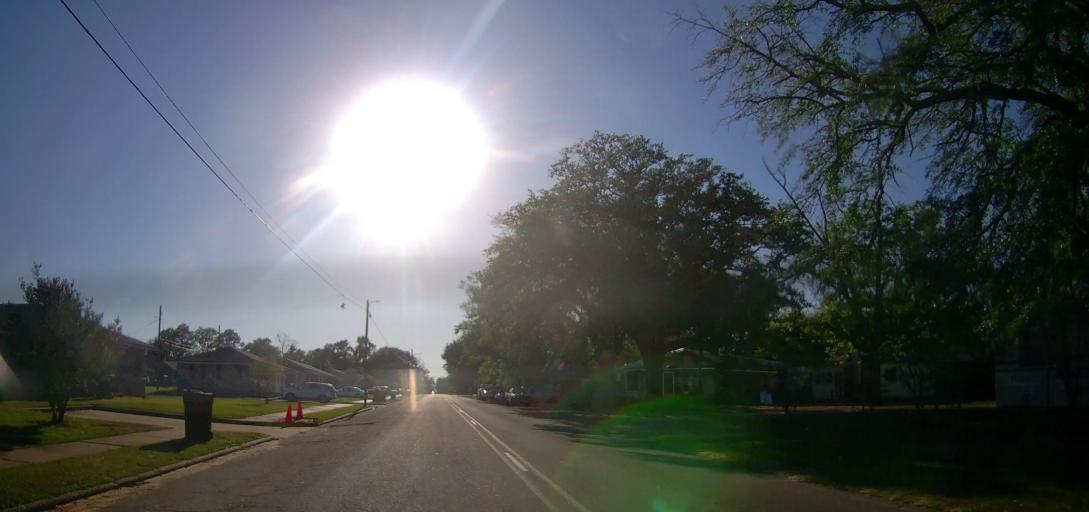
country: US
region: Georgia
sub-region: Ben Hill County
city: Fitzgerald
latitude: 31.7059
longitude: -83.2466
